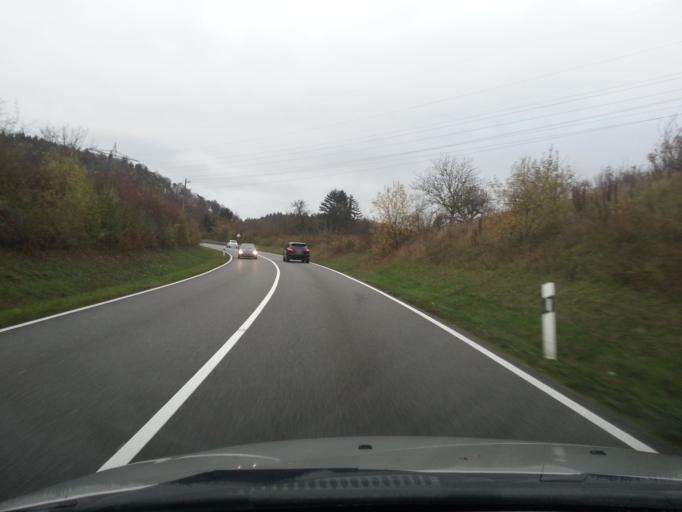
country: DE
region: Baden-Wuerttemberg
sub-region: Karlsruhe Region
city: Leimen
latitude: 49.3559
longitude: 8.7011
